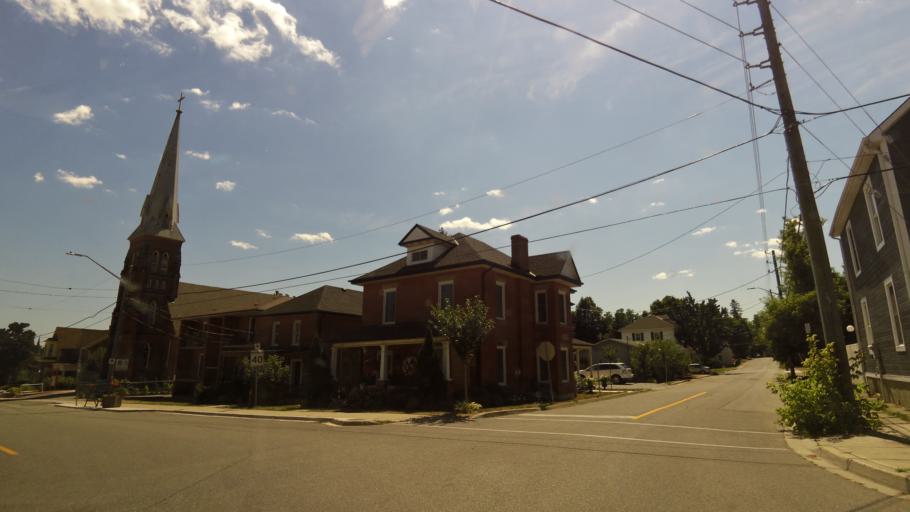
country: CA
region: Ontario
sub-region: Halton
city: Milton
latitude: 43.6515
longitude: -79.9288
